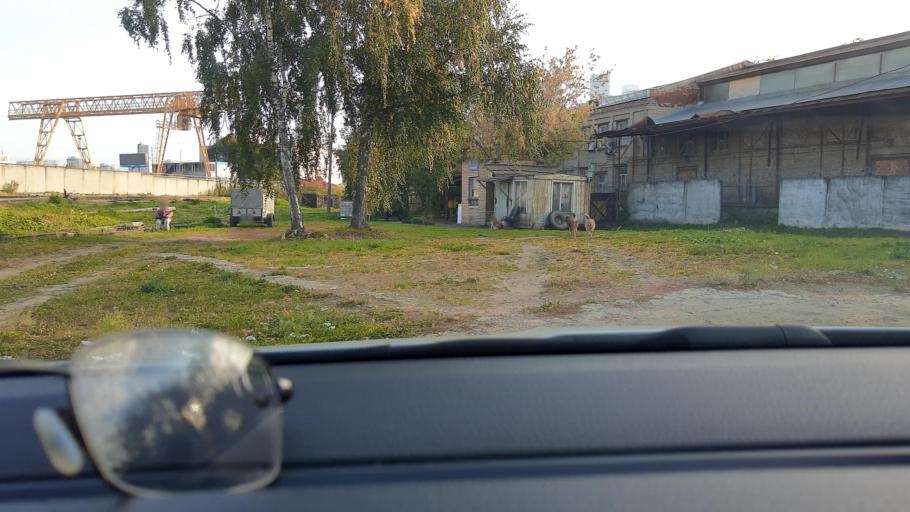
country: RU
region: Moskovskaya
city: Presnenskiy
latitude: 55.7693
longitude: 37.5346
